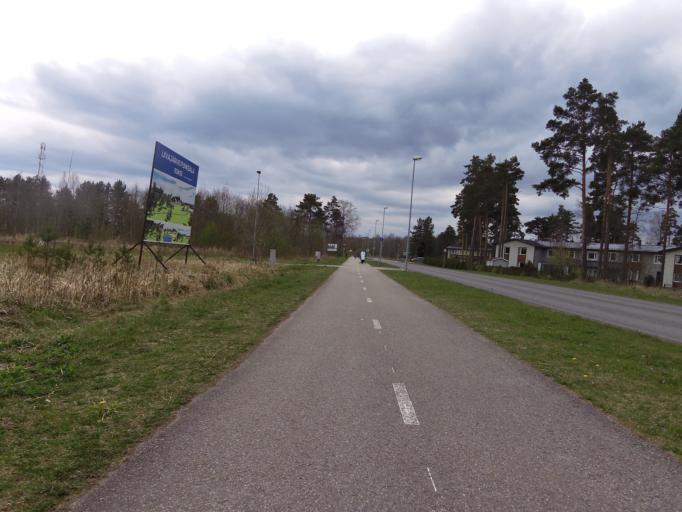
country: EE
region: Harju
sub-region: Kiili vald
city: Kiili
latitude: 59.3601
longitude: 24.8136
